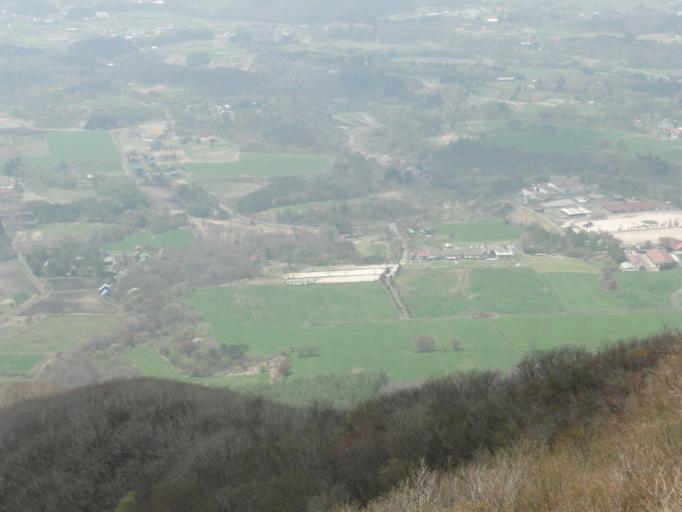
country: JP
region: Tottori
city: Kurayoshi
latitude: 35.3184
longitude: 133.6576
